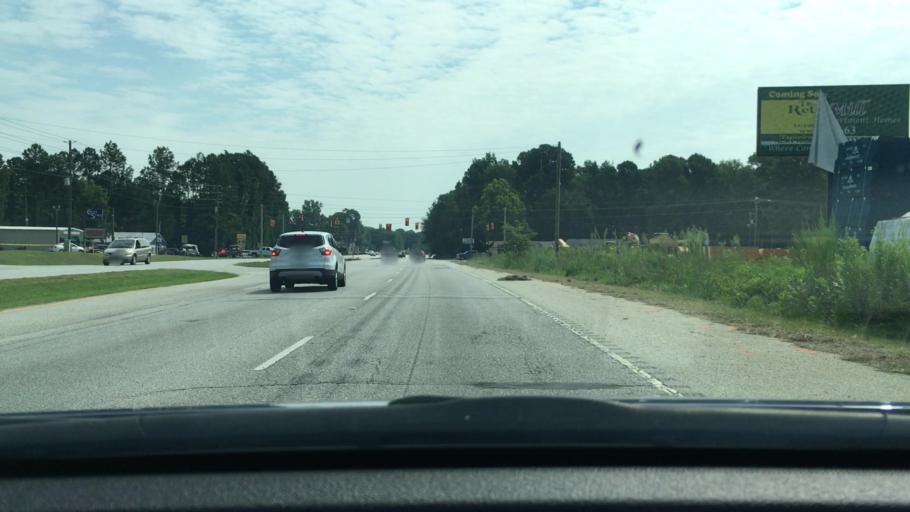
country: US
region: South Carolina
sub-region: Sumter County
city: Cherryvale
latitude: 33.9622
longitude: -80.4224
